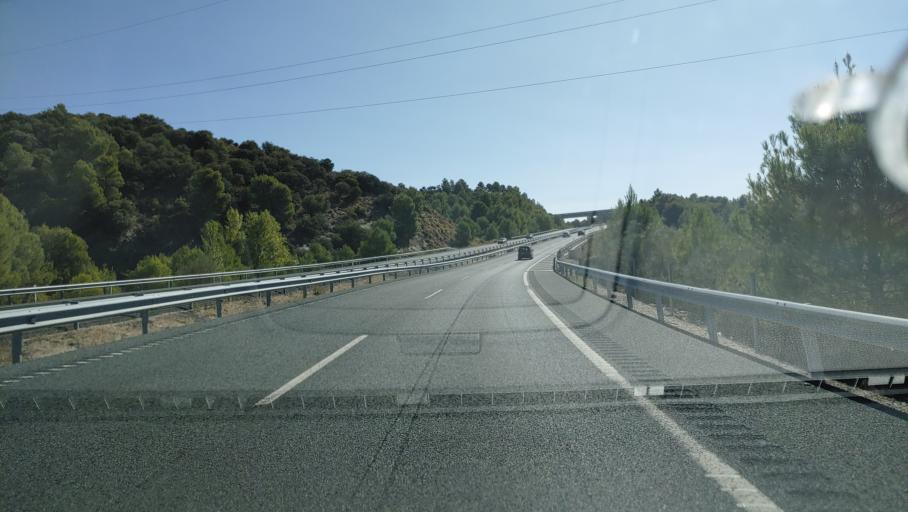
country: ES
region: Andalusia
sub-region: Provincia de Granada
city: Diezma
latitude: 37.3101
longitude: -3.3761
